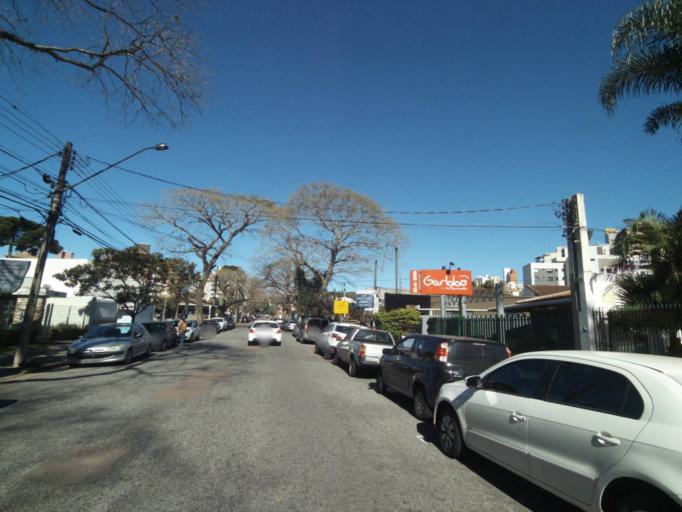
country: BR
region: Parana
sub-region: Curitiba
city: Curitiba
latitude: -25.4142
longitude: -49.2575
